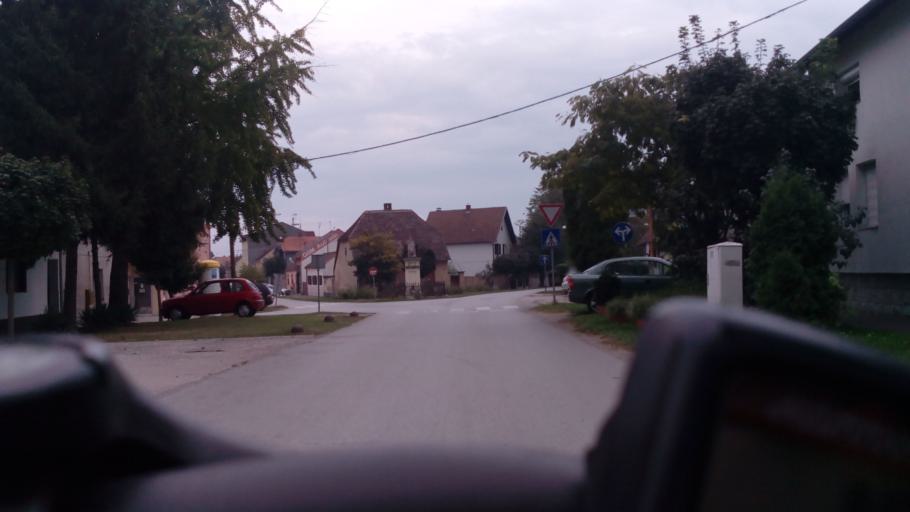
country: HR
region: Vukovarsko-Srijemska
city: Vinkovci
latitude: 45.2862
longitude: 18.8053
